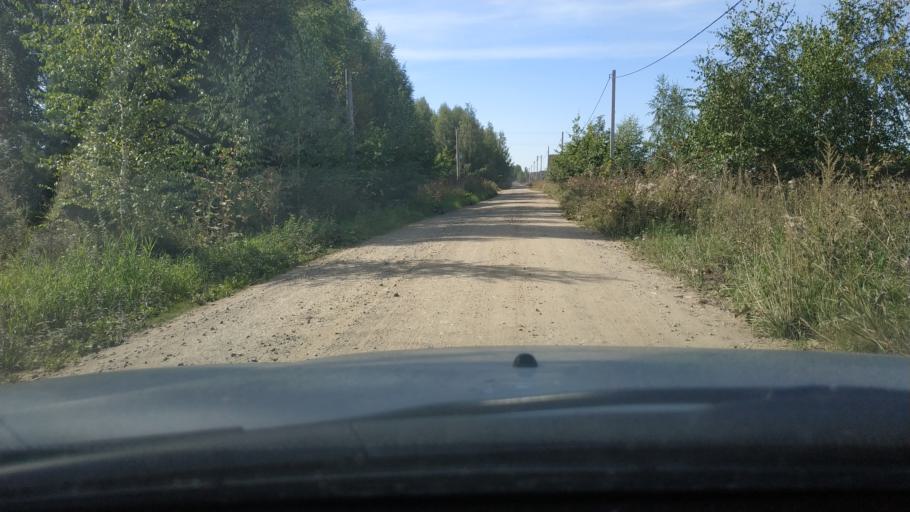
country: RU
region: Kostroma
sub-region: Kostromskoy Rayon
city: Kostroma
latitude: 57.7789
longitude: 40.7465
